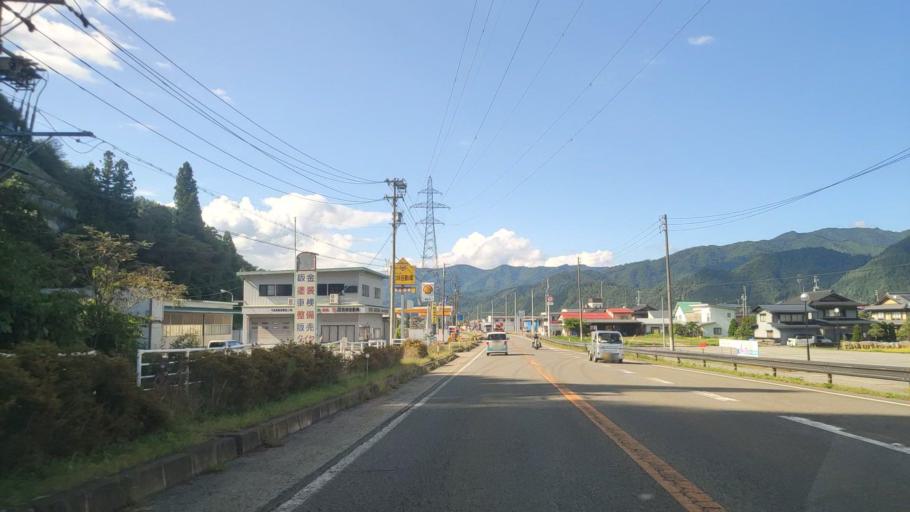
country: JP
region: Gifu
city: Takayama
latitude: 36.2310
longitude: 137.1806
